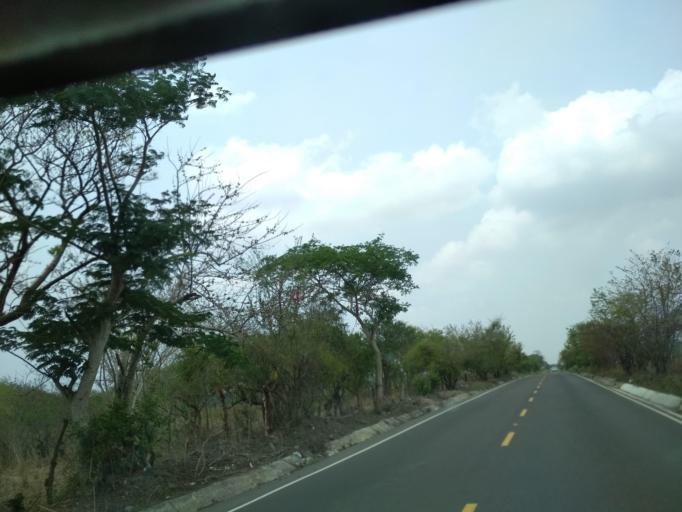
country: MX
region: Veracruz
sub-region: Veracruz
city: Delfino Victoria (Santa Fe)
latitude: 19.1525
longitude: -96.2962
